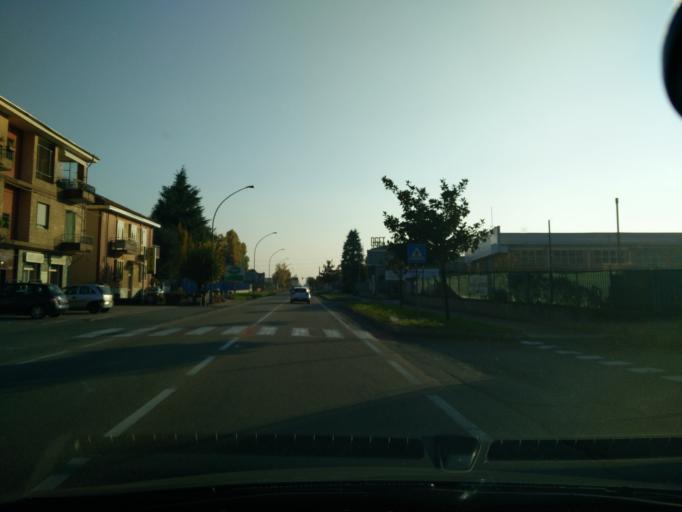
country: IT
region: Piedmont
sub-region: Provincia di Torino
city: Leini
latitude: 45.1645
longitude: 7.7115
